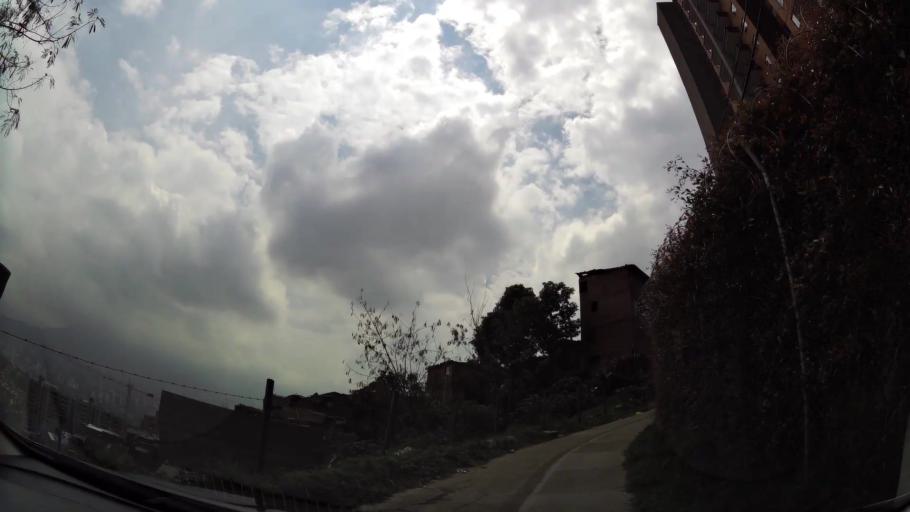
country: CO
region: Antioquia
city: Itagui
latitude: 6.1956
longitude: -75.6003
